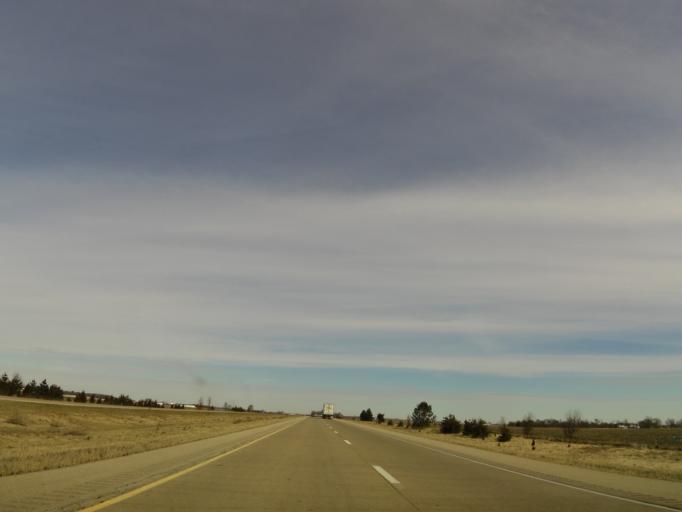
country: US
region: Illinois
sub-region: LaSalle County
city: La Salle
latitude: 41.4297
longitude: -89.0585
